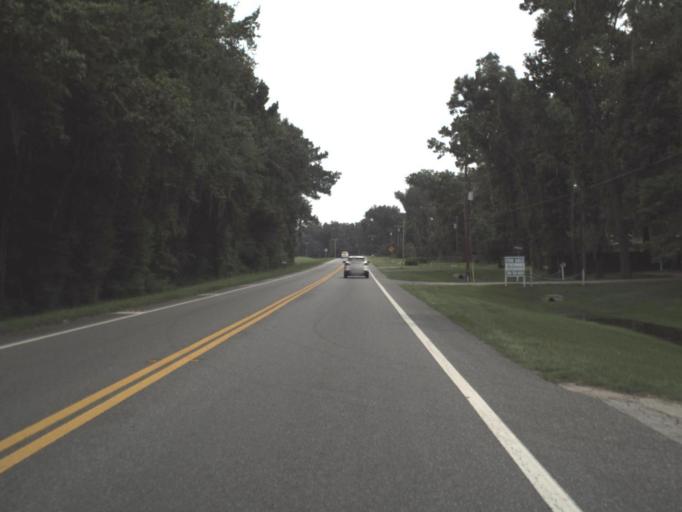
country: US
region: Florida
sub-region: Columbia County
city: Watertown
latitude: 30.0919
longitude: -82.6021
